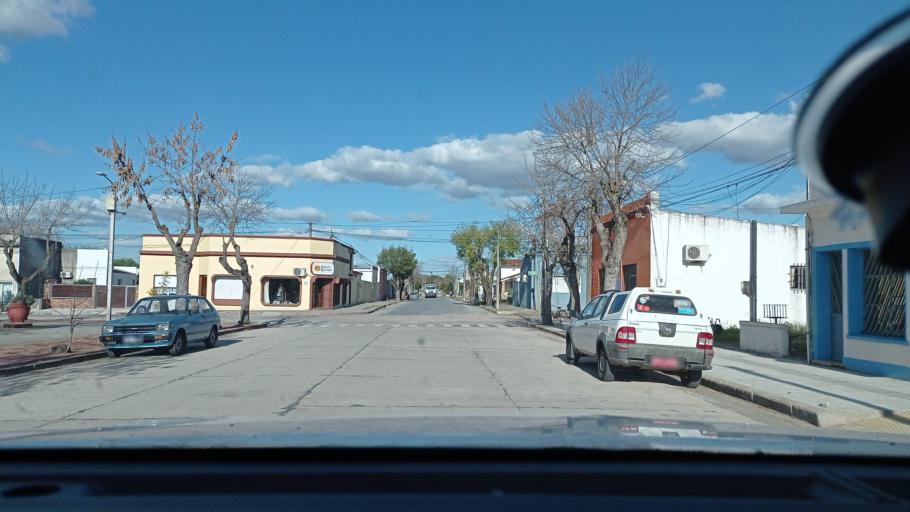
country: UY
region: Florida
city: Casupa
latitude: -34.1012
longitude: -55.6516
